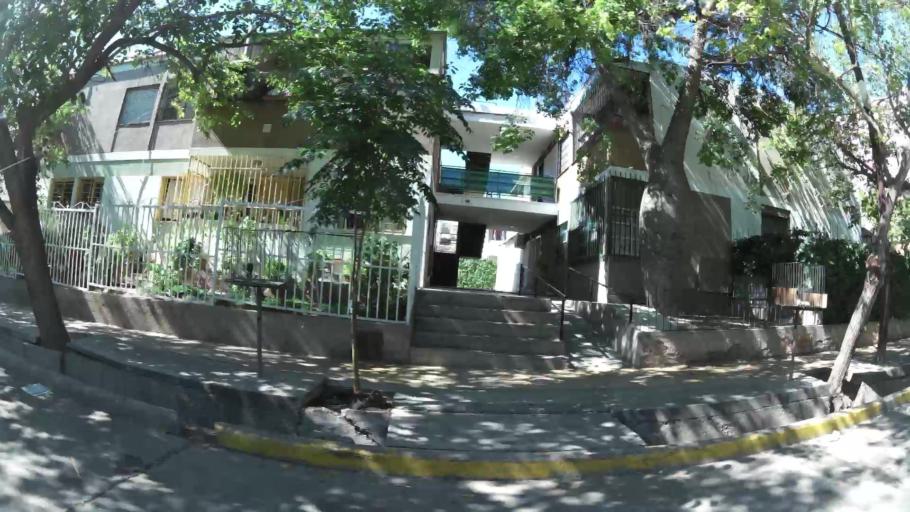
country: AR
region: Mendoza
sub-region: Departamento de Godoy Cruz
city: Godoy Cruz
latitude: -32.9103
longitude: -68.8734
